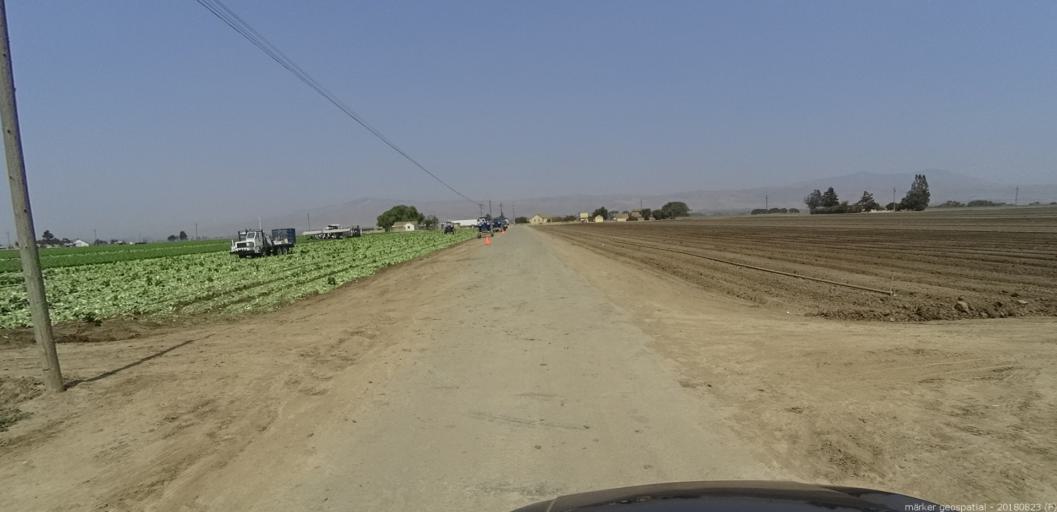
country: US
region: California
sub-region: Monterey County
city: Soledad
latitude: 36.3987
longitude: -121.3425
